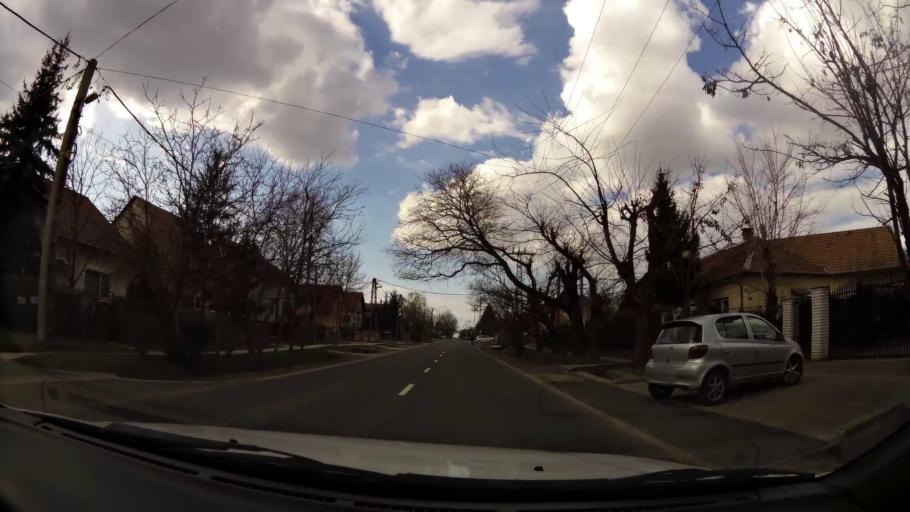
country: HU
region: Budapest
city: Budapest XVII. keruelet
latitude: 47.4980
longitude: 19.2710
